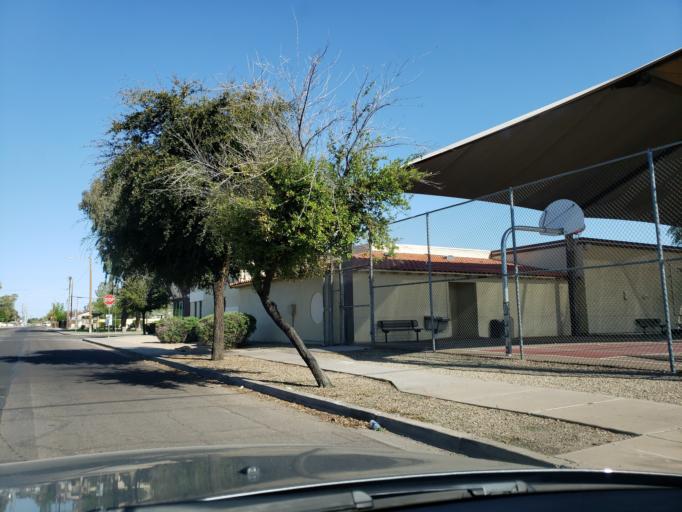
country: US
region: Arizona
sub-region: Maricopa County
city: Glendale
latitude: 33.5349
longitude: -112.1756
